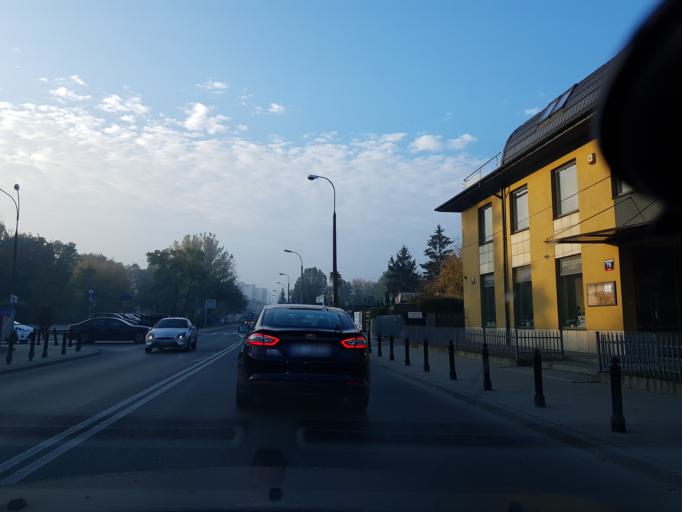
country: PL
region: Masovian Voivodeship
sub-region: Warszawa
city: Targowek
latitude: 52.2764
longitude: 21.0430
